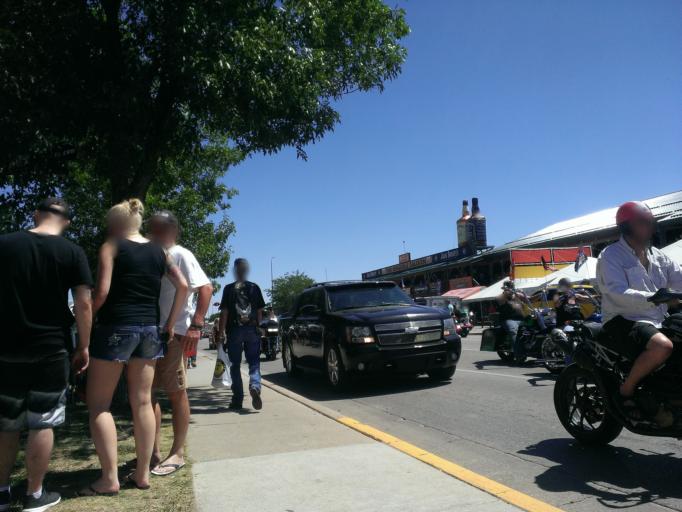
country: US
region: South Dakota
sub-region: Meade County
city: Sturgis
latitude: 44.4157
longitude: -103.5126
